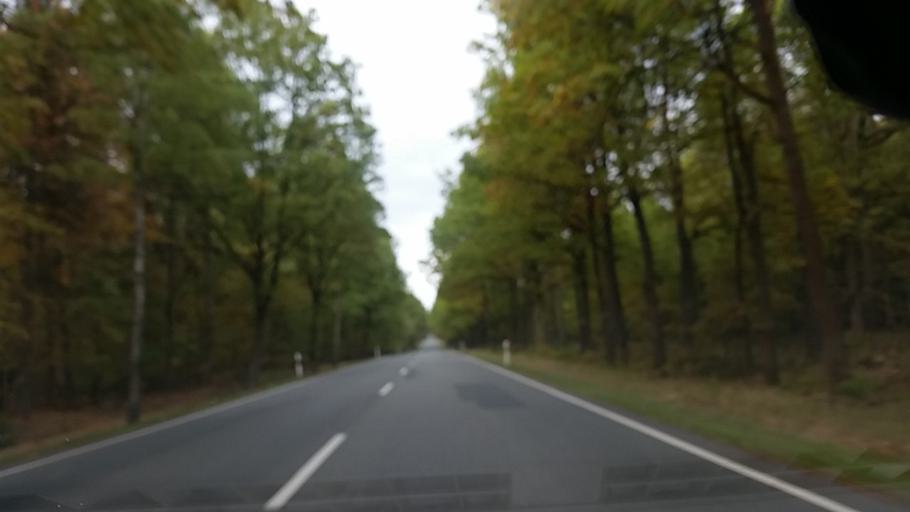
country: DE
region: Lower Saxony
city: Sprakensehl
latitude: 52.7979
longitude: 10.4889
